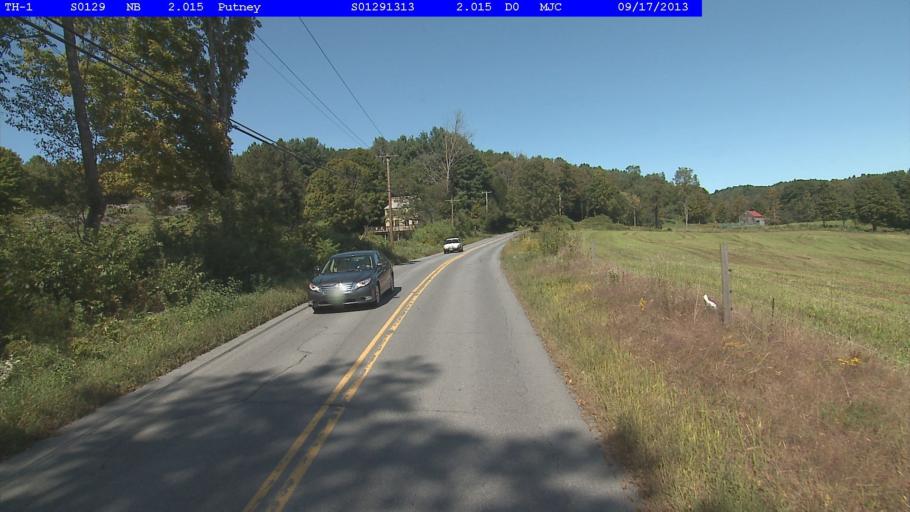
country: US
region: New Hampshire
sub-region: Cheshire County
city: Westmoreland
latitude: 43.0016
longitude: -72.5327
